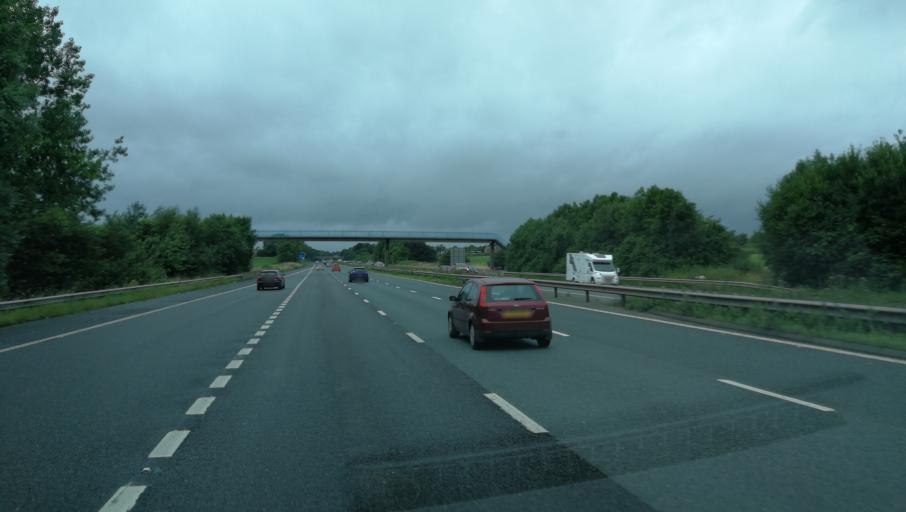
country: GB
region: England
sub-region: Borough of Wigan
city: Tyldesley
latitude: 53.5460
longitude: -2.4552
